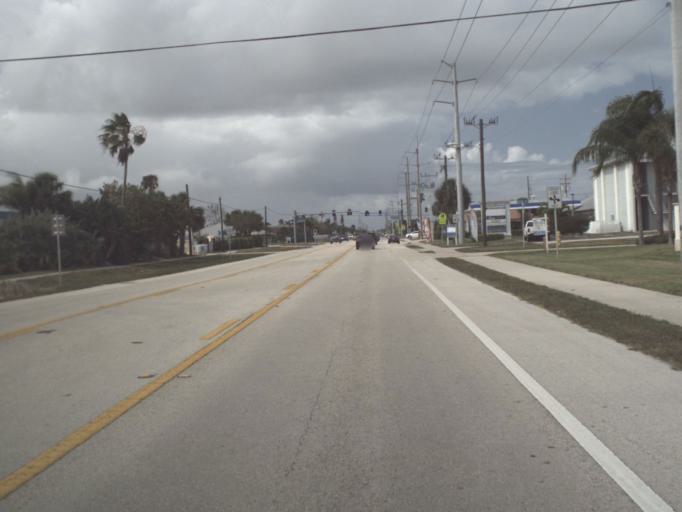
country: US
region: Florida
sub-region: Brevard County
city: Satellite Beach
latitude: 28.1812
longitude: -80.6061
